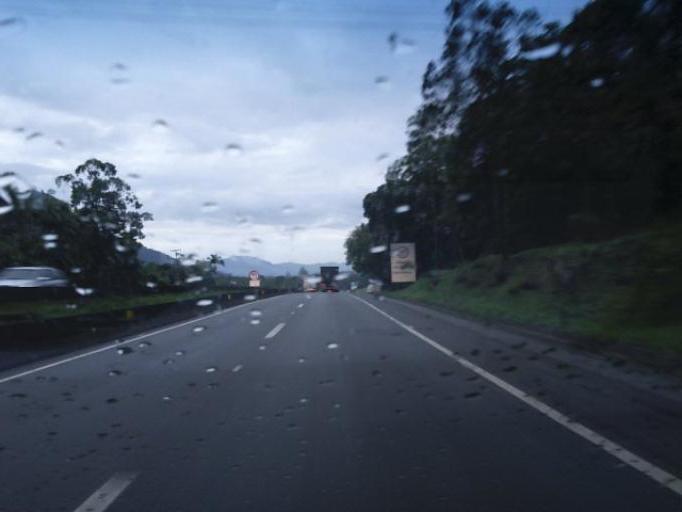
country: BR
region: Parana
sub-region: Guaratuba
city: Guaratuba
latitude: -25.9697
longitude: -48.8935
